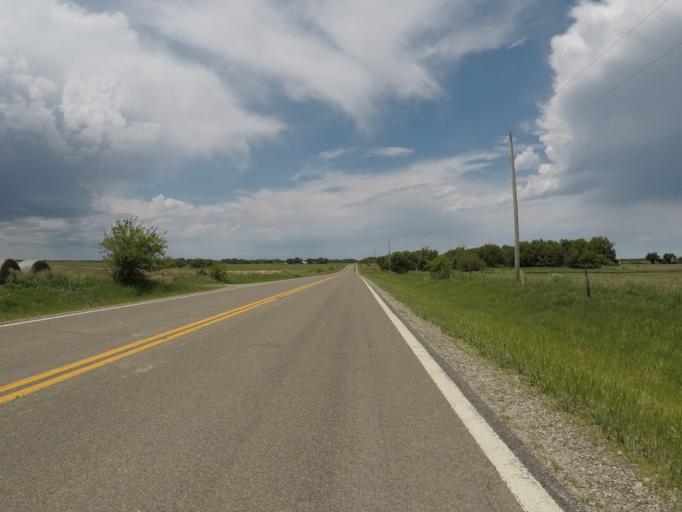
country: US
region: Kansas
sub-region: Wabaunsee County
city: Alma
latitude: 38.8547
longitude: -96.4156
